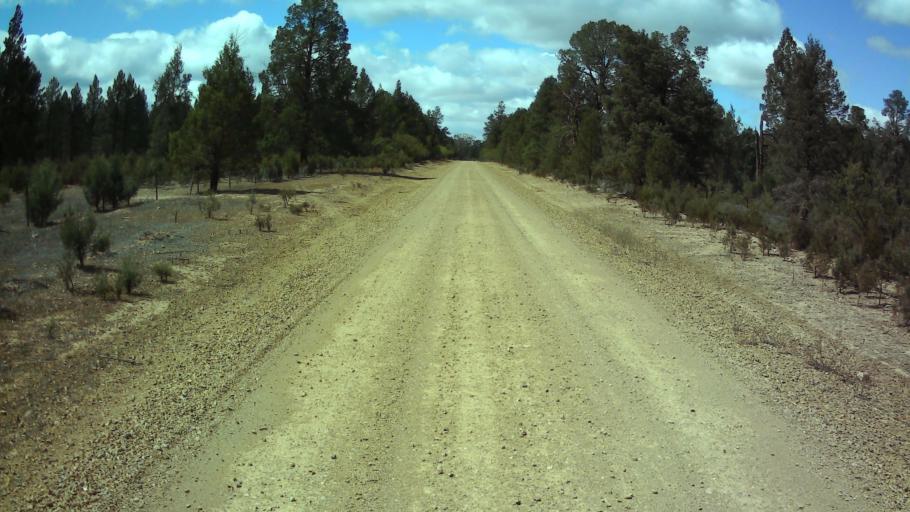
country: AU
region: New South Wales
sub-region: Weddin
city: Grenfell
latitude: -33.9118
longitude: 147.9202
